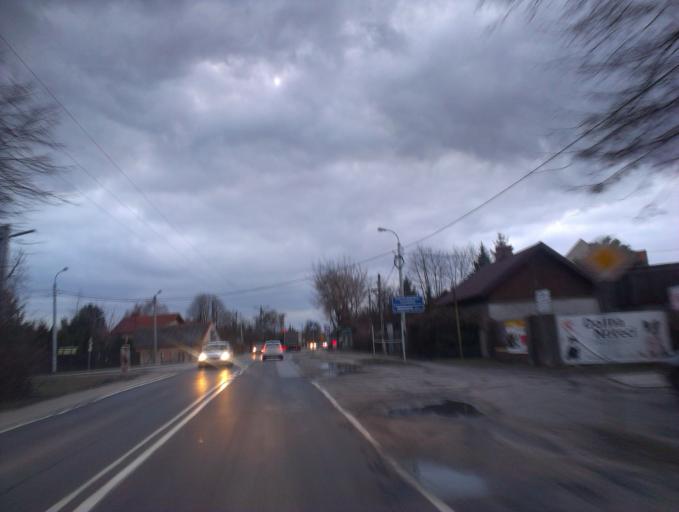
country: PL
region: Masovian Voivodeship
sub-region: Powiat piaseczynski
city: Konstancin-Jeziorna
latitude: 52.0858
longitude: 21.0953
